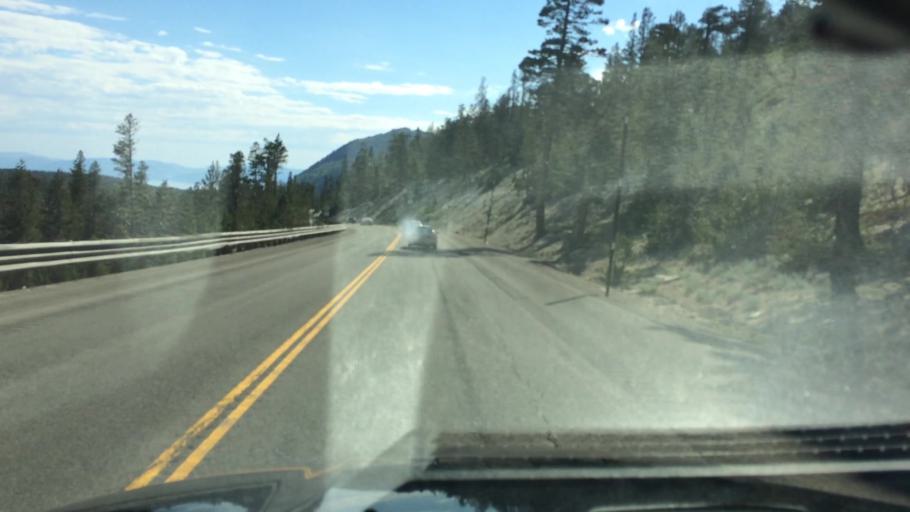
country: US
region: Nevada
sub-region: Washoe County
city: Incline Village
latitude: 39.3121
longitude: -119.8982
